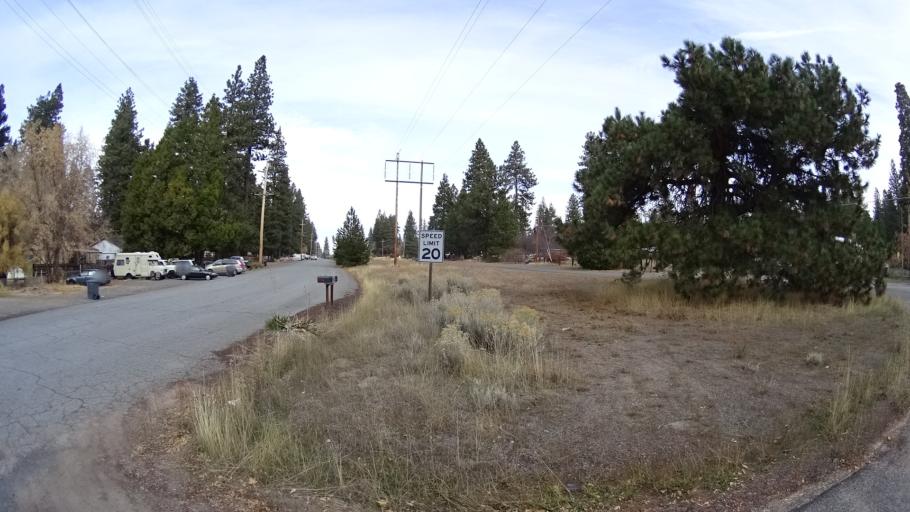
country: US
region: California
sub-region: Siskiyou County
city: Weed
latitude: 41.4453
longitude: -122.3622
